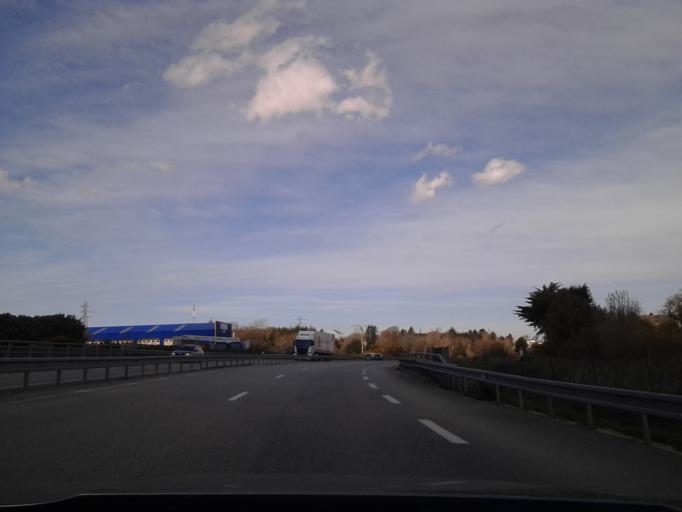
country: FR
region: Lower Normandy
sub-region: Departement de la Manche
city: La Glacerie
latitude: 49.5873
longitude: -1.5964
